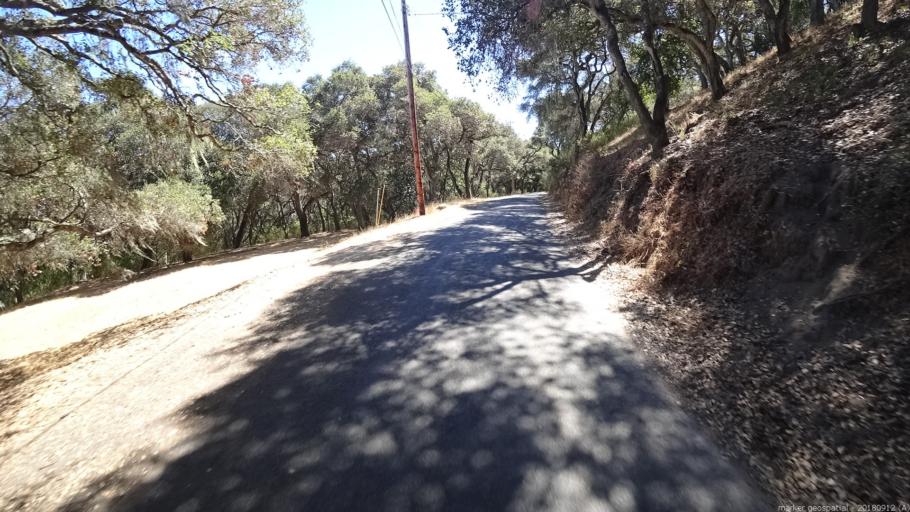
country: US
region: California
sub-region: Monterey County
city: Carmel Valley Village
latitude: 36.4687
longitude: -121.7316
